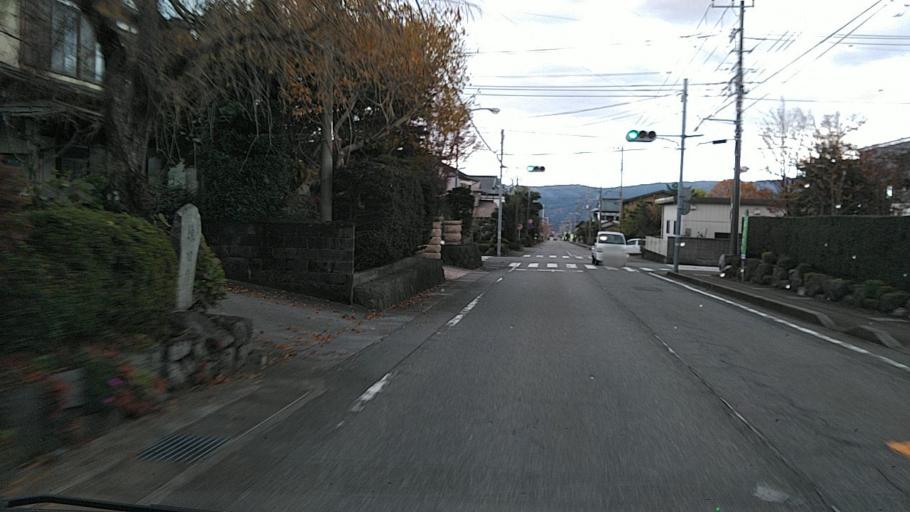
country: JP
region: Shizuoka
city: Gotemba
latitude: 35.3362
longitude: 138.9383
